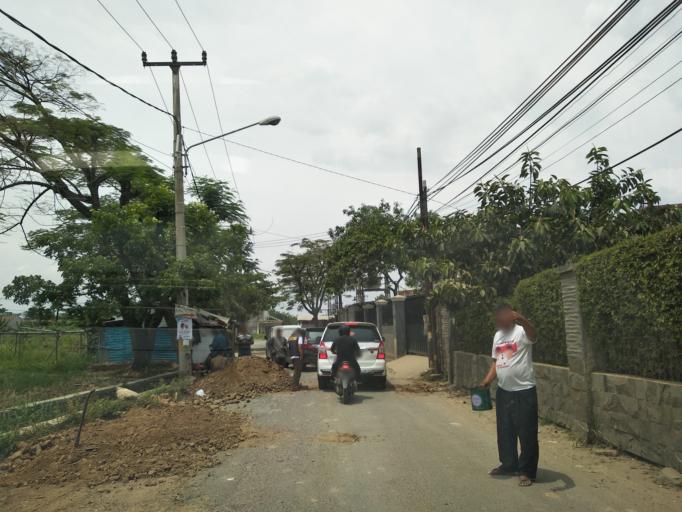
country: ID
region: West Java
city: Pameungpeuk
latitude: -6.9699
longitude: 107.6385
